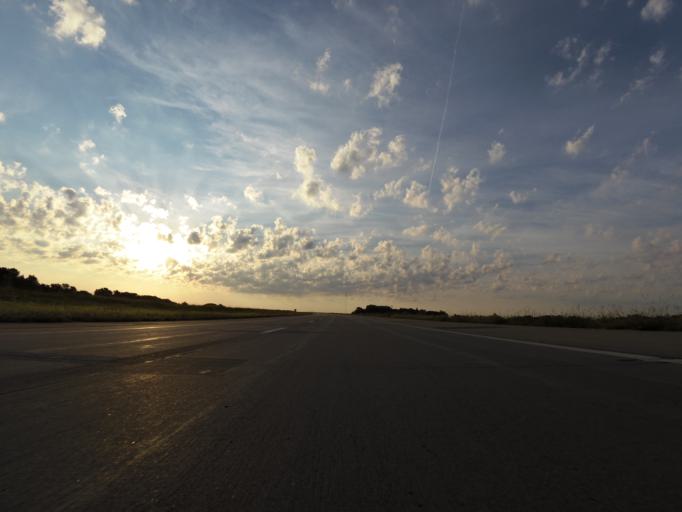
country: US
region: Kansas
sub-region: Reno County
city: Haven
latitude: 37.8747
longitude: -97.6970
